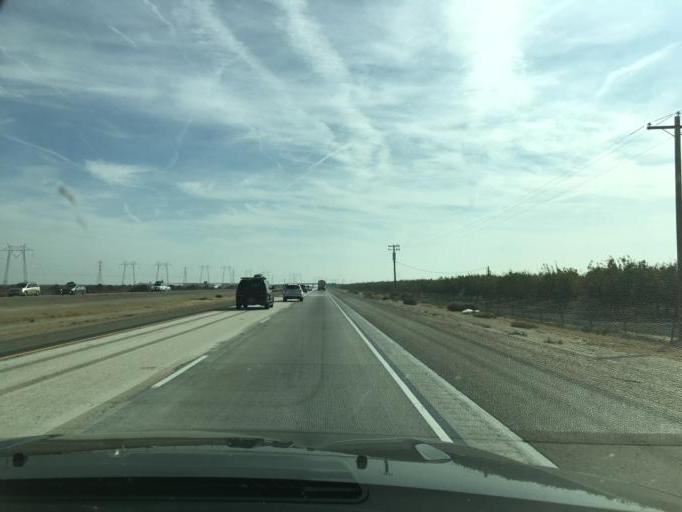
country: US
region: California
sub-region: Kern County
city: Buttonwillow
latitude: 35.5085
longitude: -119.5443
